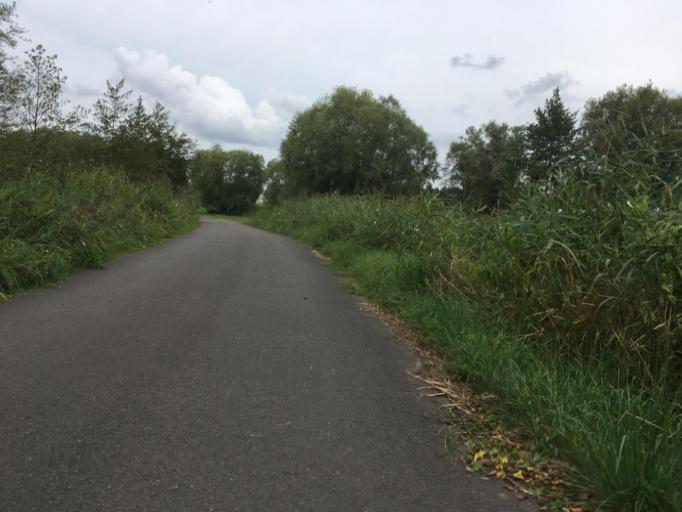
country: DE
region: Brandenburg
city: Prenzlau
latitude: 53.2736
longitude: 13.8463
